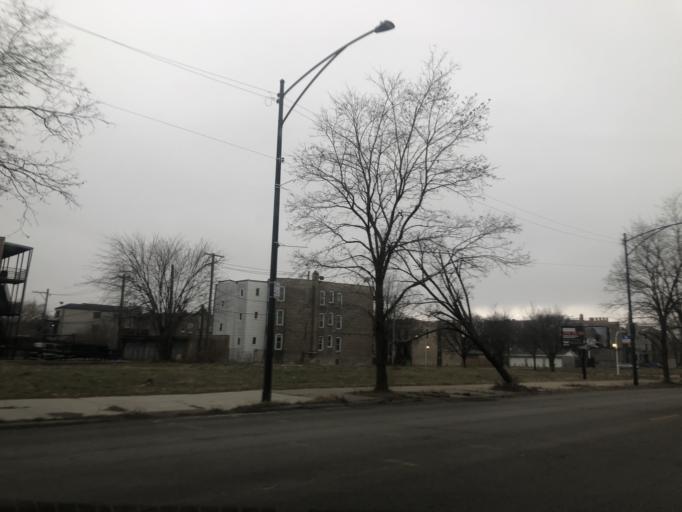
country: US
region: Illinois
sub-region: Cook County
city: Chicago
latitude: 41.7806
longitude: -87.5995
